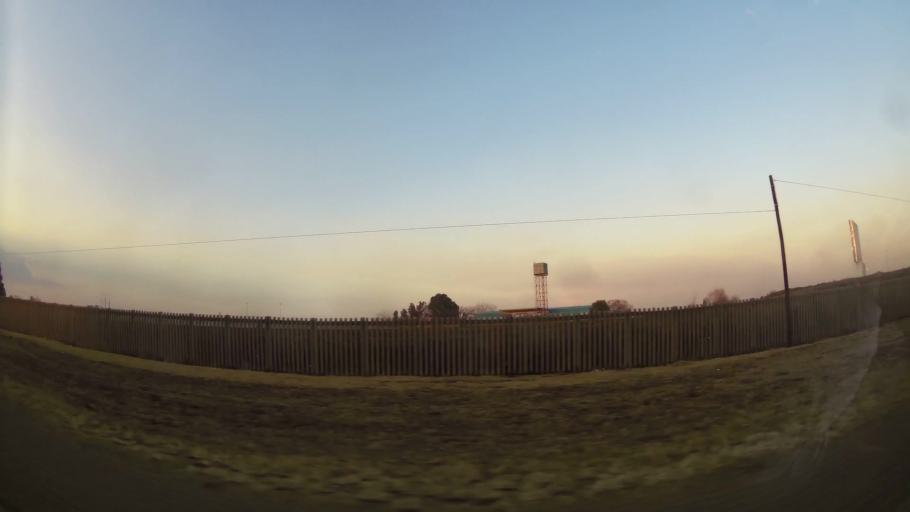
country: ZA
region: Gauteng
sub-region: Ekurhuleni Metropolitan Municipality
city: Springs
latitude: -26.2888
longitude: 28.4057
